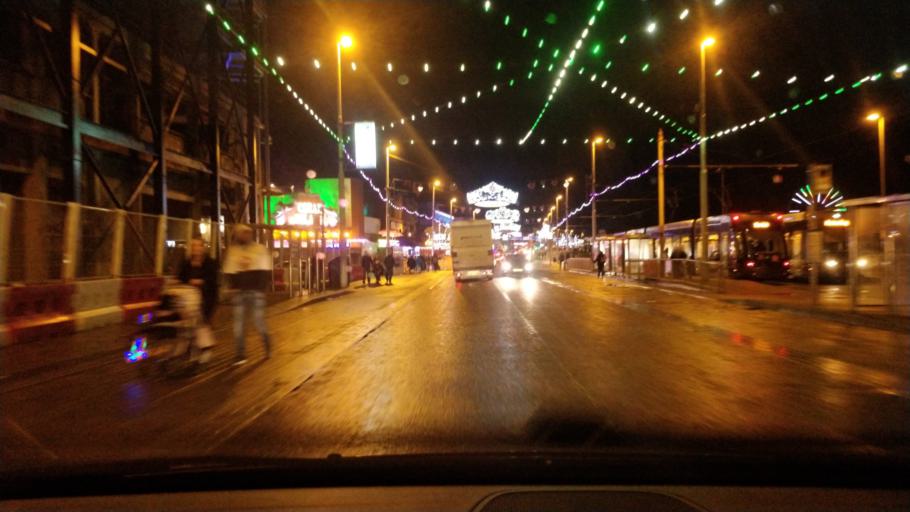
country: GB
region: England
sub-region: Blackpool
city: Blackpool
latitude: 53.8150
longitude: -3.0557
